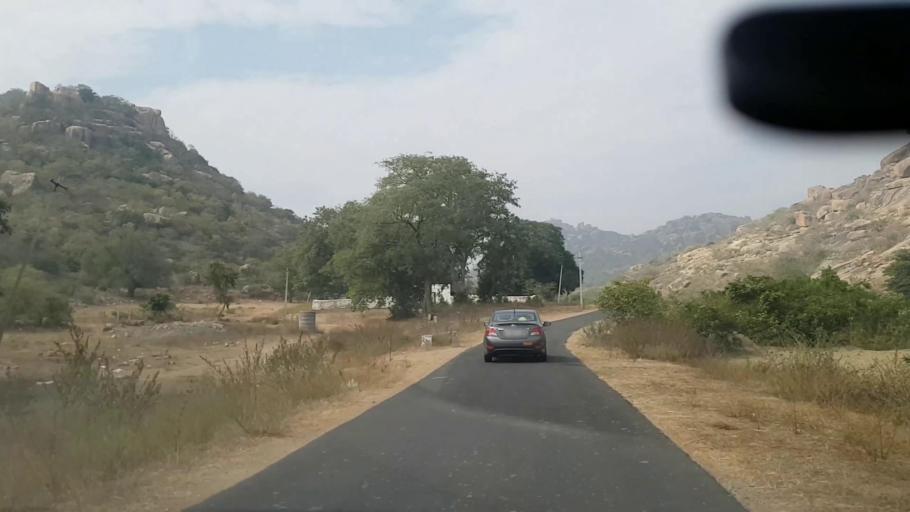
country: IN
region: Telangana
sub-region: Rangareddi
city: Ghatkesar
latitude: 17.1720
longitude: 78.8135
